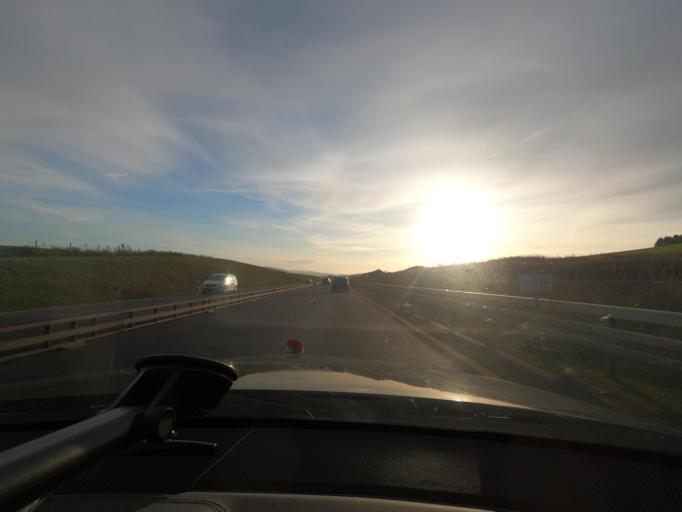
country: DE
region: Lower Saxony
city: Northeim
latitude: 51.7536
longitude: 10.0115
